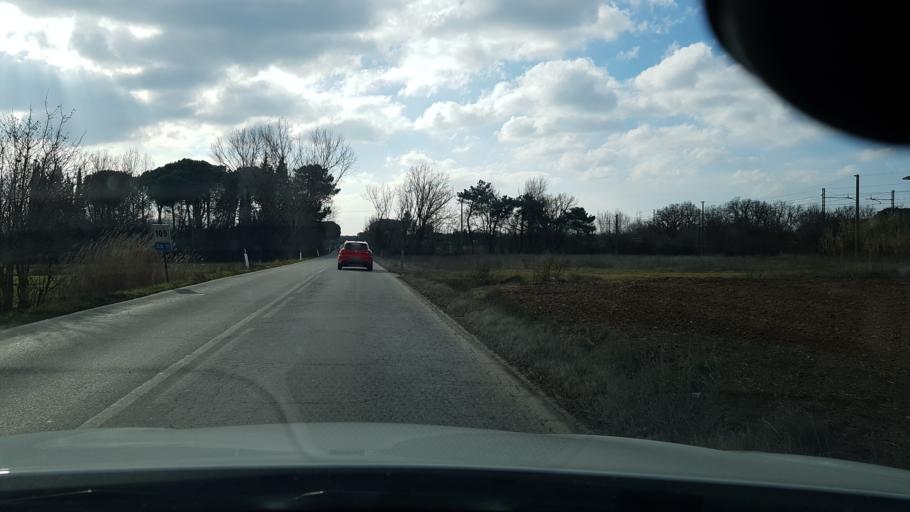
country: IT
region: Tuscany
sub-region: Province of Arezzo
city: Terontola
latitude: 43.1724
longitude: 12.0141
